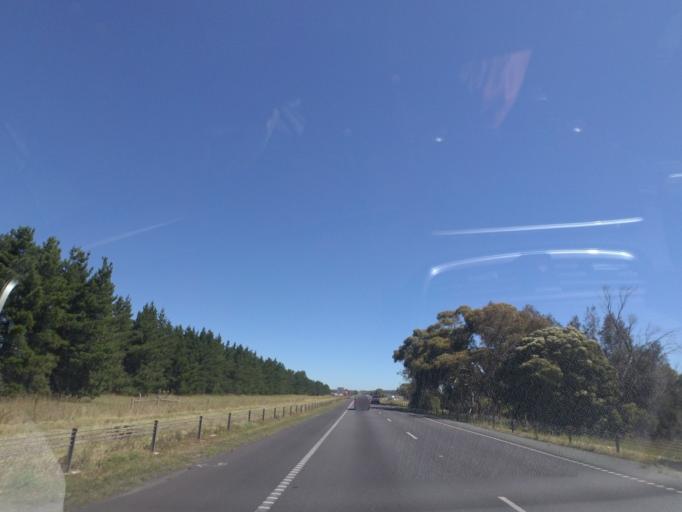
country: AU
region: Victoria
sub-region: Hume
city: Craigieburn
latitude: -37.5207
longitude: 144.9489
